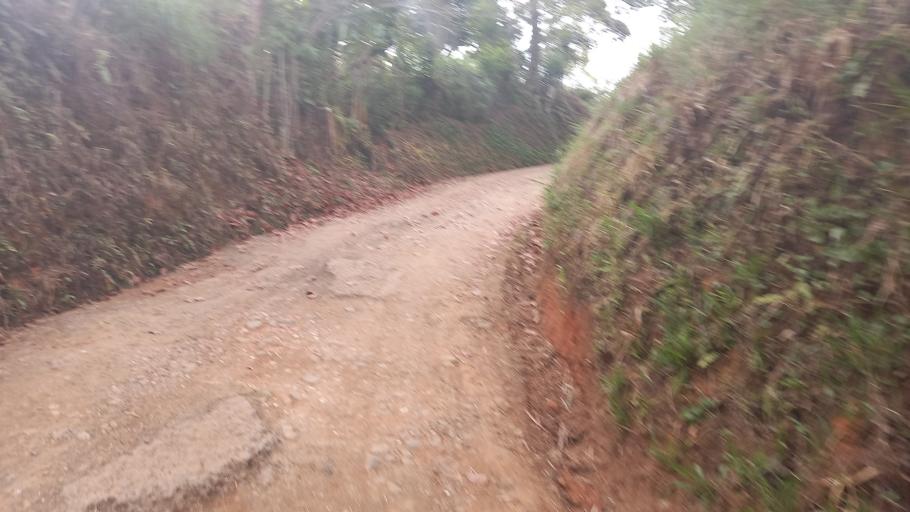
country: CO
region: Antioquia
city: Santa Barbara
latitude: 5.8296
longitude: -75.5765
